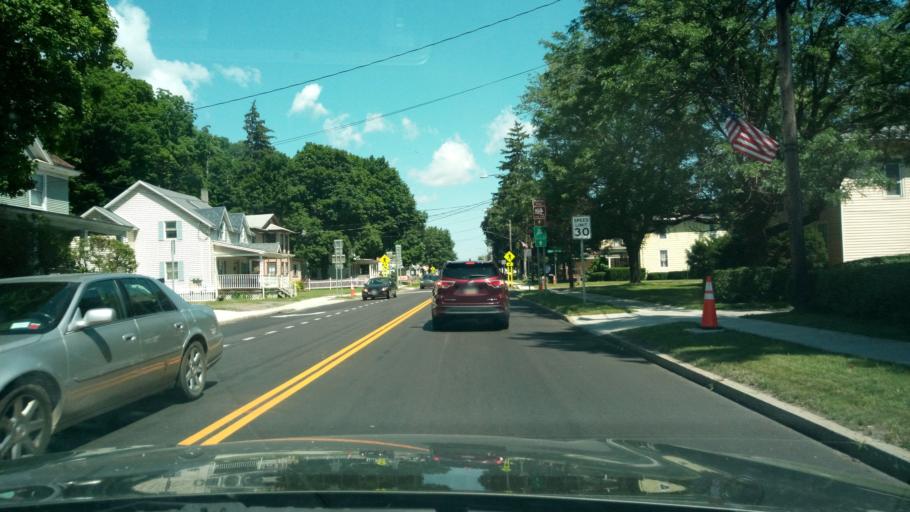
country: US
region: New York
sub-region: Schuyler County
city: Watkins Glen
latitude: 42.3723
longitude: -76.8690
